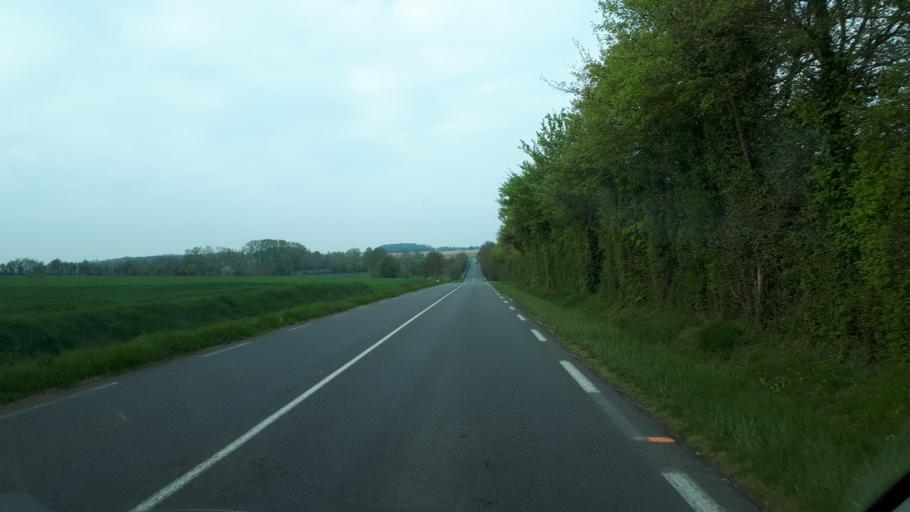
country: FR
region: Centre
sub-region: Departement du Cher
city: Rians
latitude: 47.1932
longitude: 2.5612
